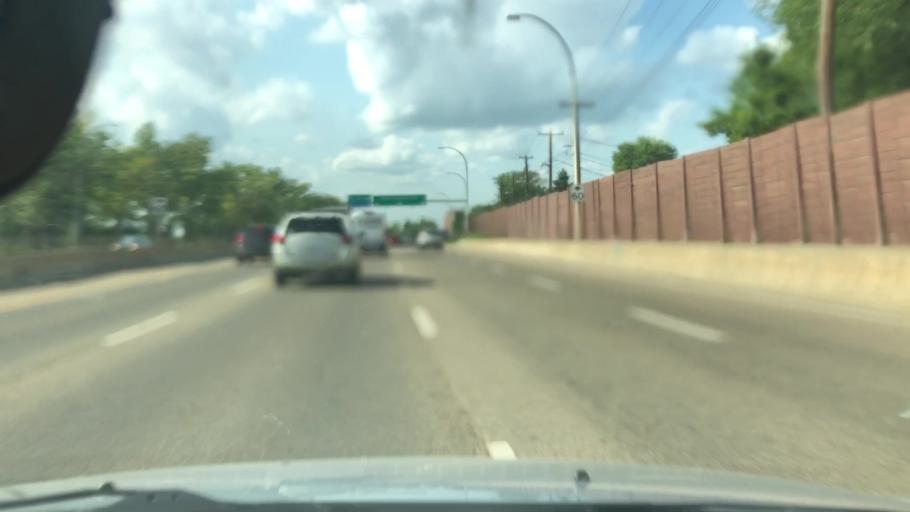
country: CA
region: Alberta
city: Edmonton
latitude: 53.5653
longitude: -113.4490
